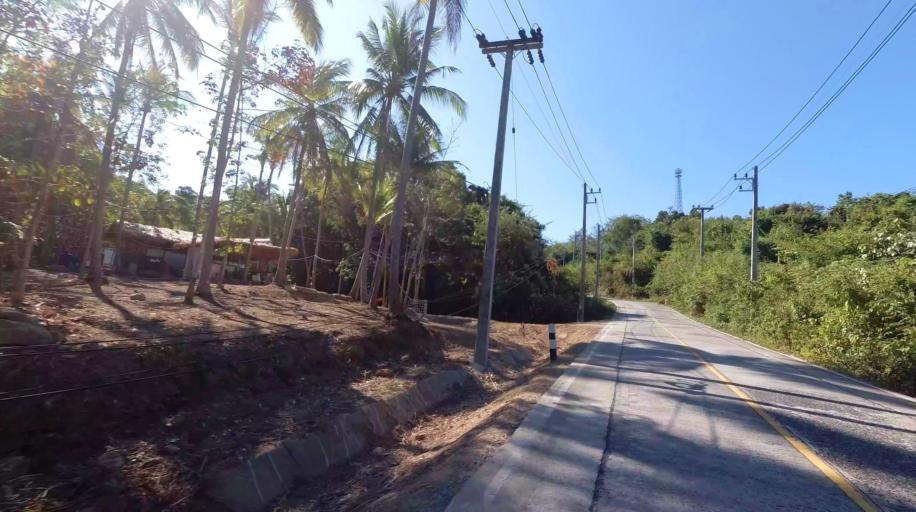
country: TH
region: Trat
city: Ko Kut
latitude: 11.6165
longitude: 102.5437
